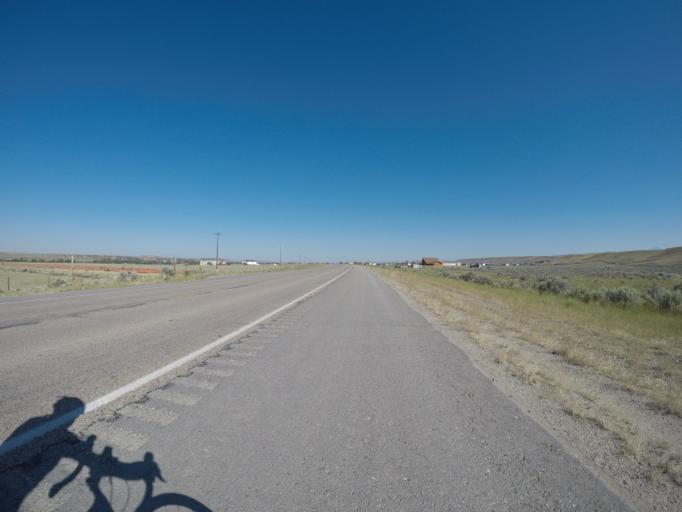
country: US
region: Wyoming
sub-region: Sublette County
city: Pinedale
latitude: 42.7611
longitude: -109.7347
